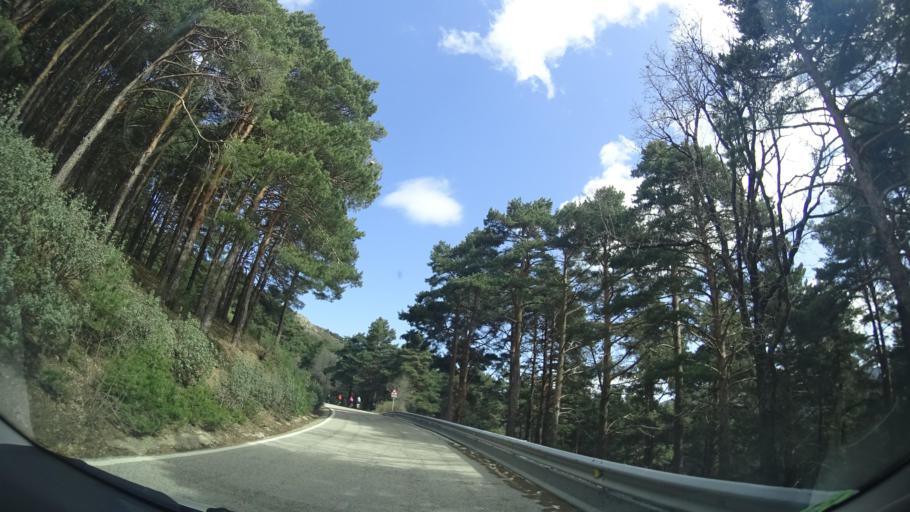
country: ES
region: Madrid
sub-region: Provincia de Madrid
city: Miraflores de la Sierra
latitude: 40.8555
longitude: -3.7659
